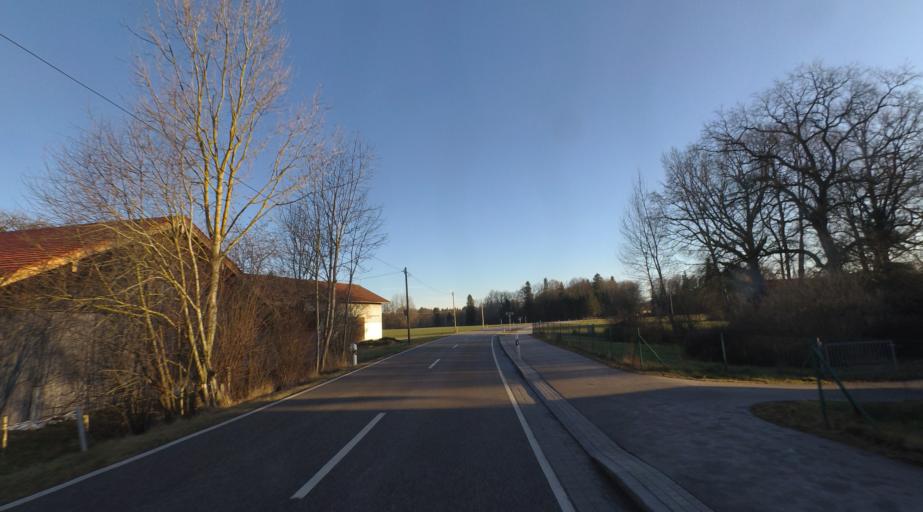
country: DE
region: Bavaria
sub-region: Upper Bavaria
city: Kirchanschoring
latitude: 47.9693
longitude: 12.8204
